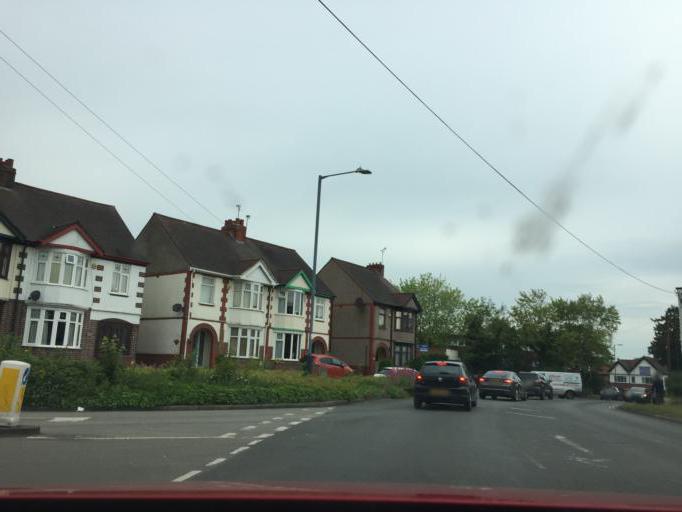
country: GB
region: England
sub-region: Warwickshire
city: Attleborough
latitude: 52.5156
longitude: -1.4579
